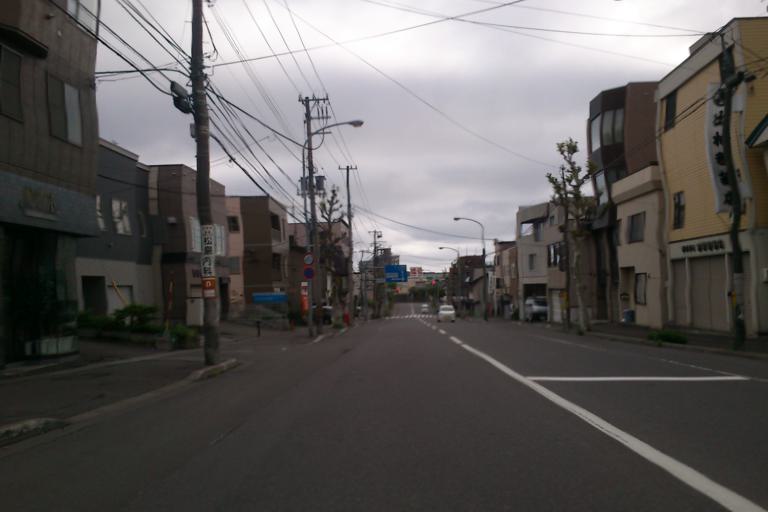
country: JP
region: Hokkaido
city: Otaru
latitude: 43.1914
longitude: 140.9910
